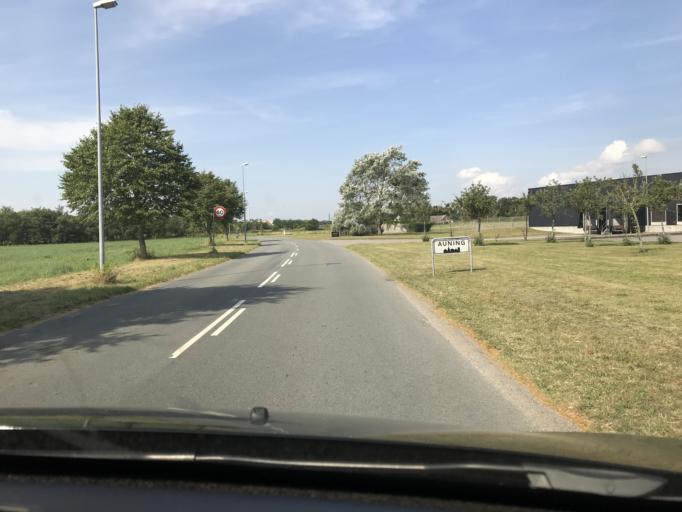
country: DK
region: Central Jutland
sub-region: Norddjurs Kommune
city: Auning
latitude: 56.4262
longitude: 10.3963
